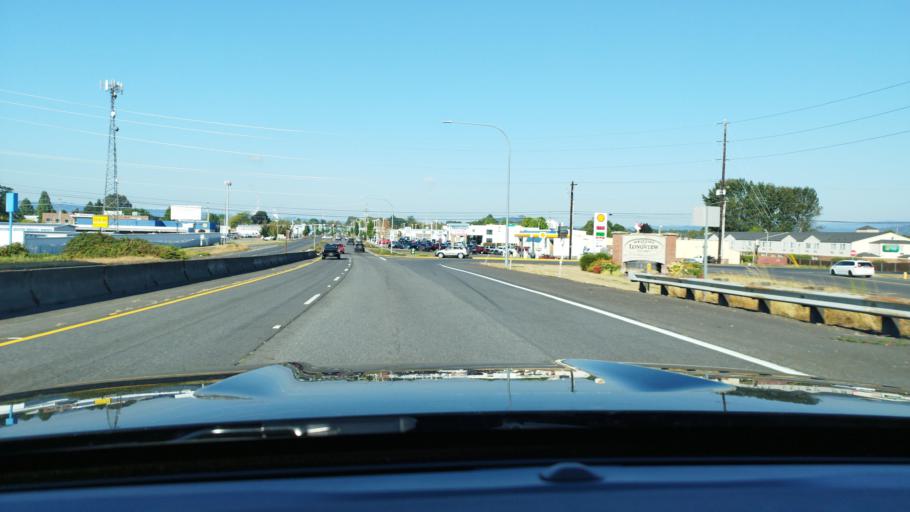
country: US
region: Washington
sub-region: Cowlitz County
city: Longview
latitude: 46.1242
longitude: -122.9296
